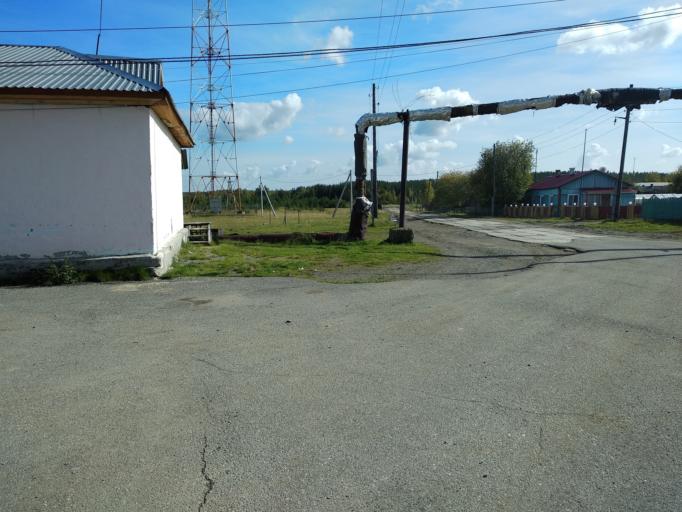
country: RU
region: Sverdlovsk
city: Karpinsk
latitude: 59.9325
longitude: 59.8105
